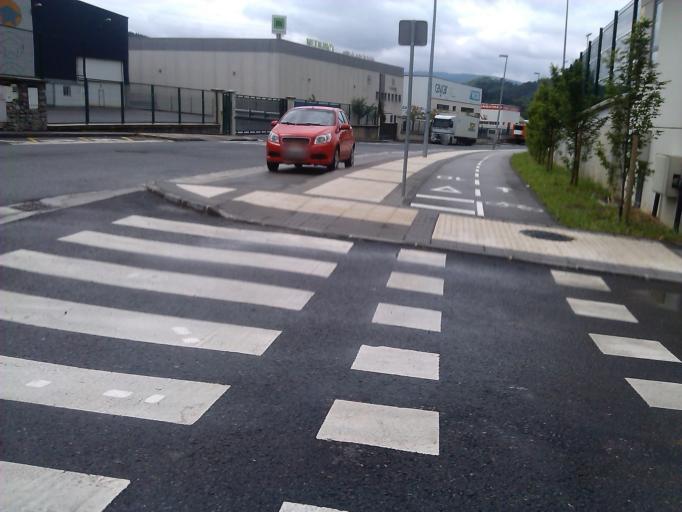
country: ES
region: Basque Country
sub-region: Provincia de Guipuzcoa
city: Urnieta
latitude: 43.2318
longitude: -2.0008
